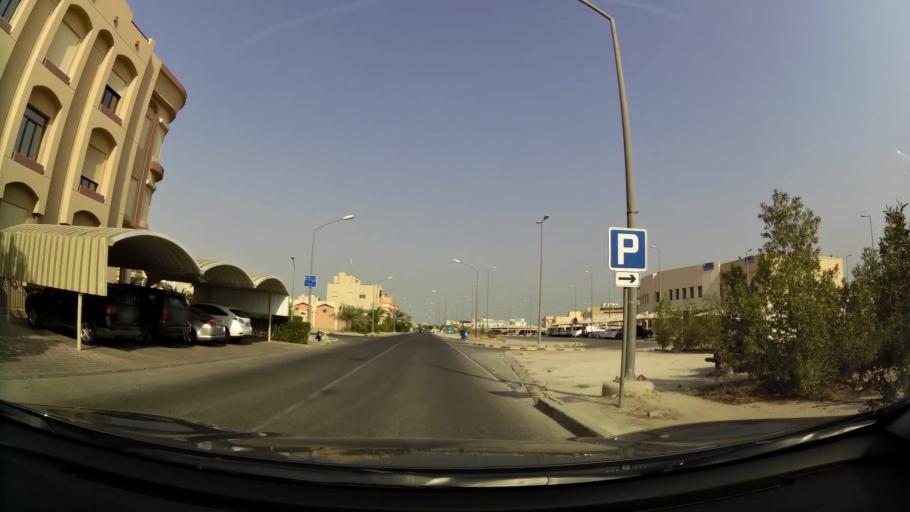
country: KW
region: Mubarak al Kabir
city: Sabah as Salim
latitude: 29.2732
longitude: 48.0420
